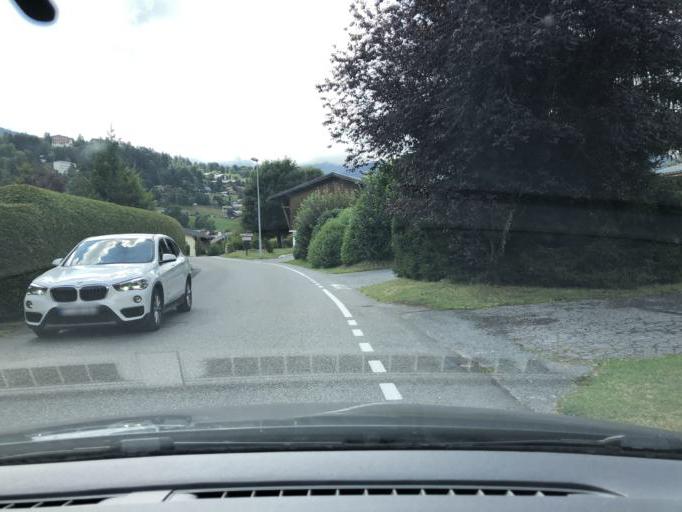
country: FR
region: Rhone-Alpes
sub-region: Departement de la Haute-Savoie
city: Megeve
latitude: 45.8686
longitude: 6.6237
